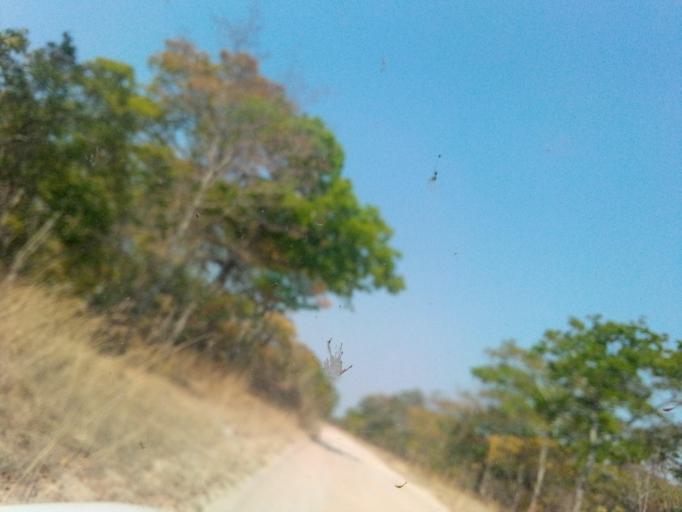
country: ZM
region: Northern
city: Mpika
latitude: -12.2255
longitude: 30.8941
